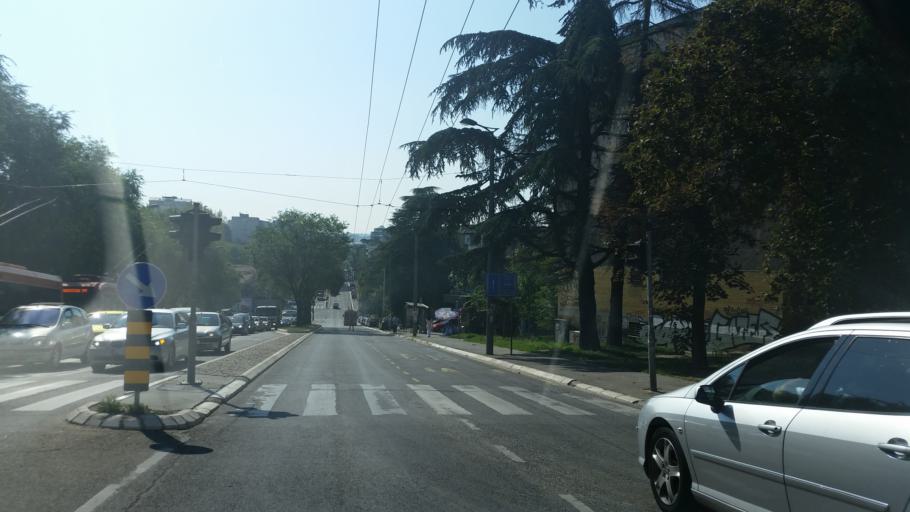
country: RS
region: Central Serbia
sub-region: Belgrade
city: Vracar
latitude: 44.7882
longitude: 20.4995
